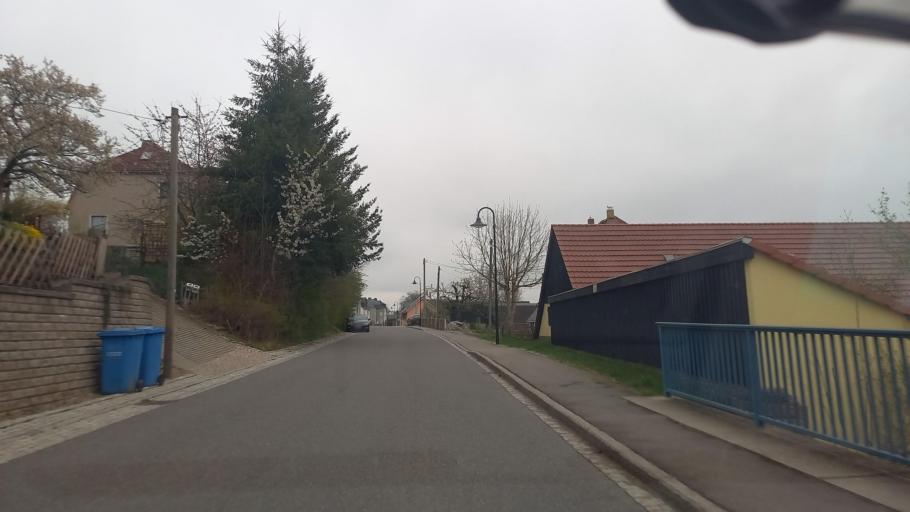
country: DE
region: Saxony
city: Reinsdorf
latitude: 50.6987
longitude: 12.5604
